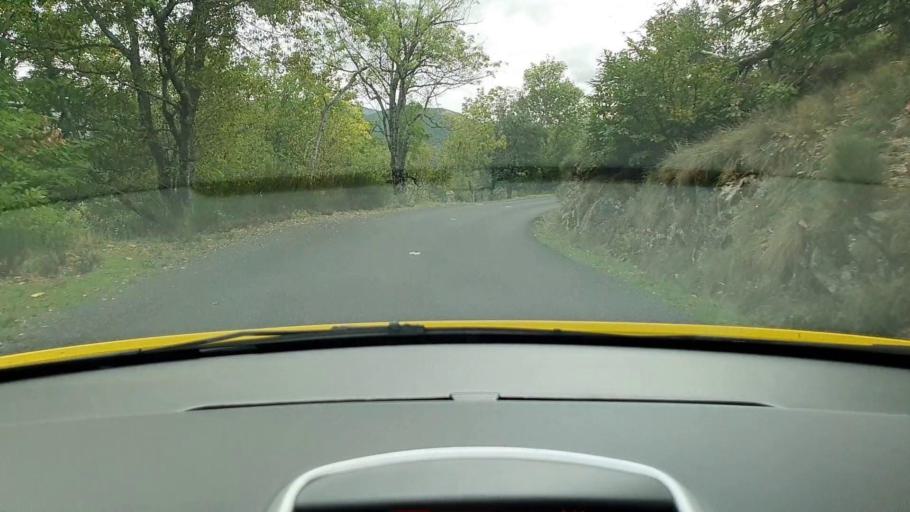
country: FR
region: Languedoc-Roussillon
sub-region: Departement de la Lozere
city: Meyrueis
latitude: 44.0709
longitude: 3.4349
